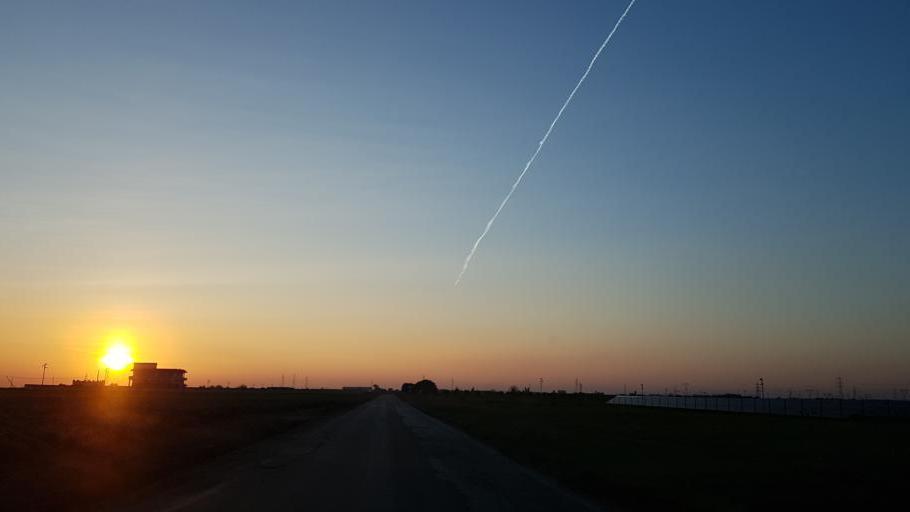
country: IT
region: Apulia
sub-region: Provincia di Brindisi
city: La Rosa
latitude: 40.5902
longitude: 17.9300
